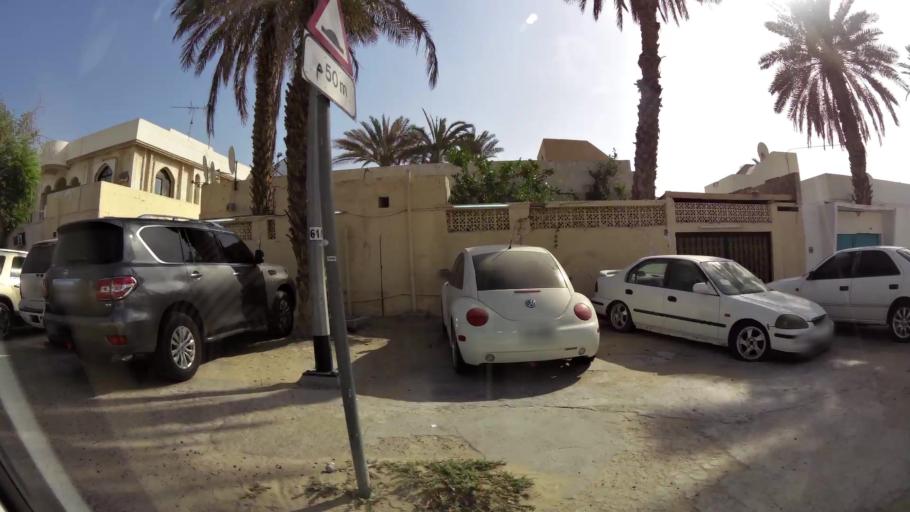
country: AE
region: Ash Shariqah
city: Sharjah
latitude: 25.2587
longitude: 55.4022
